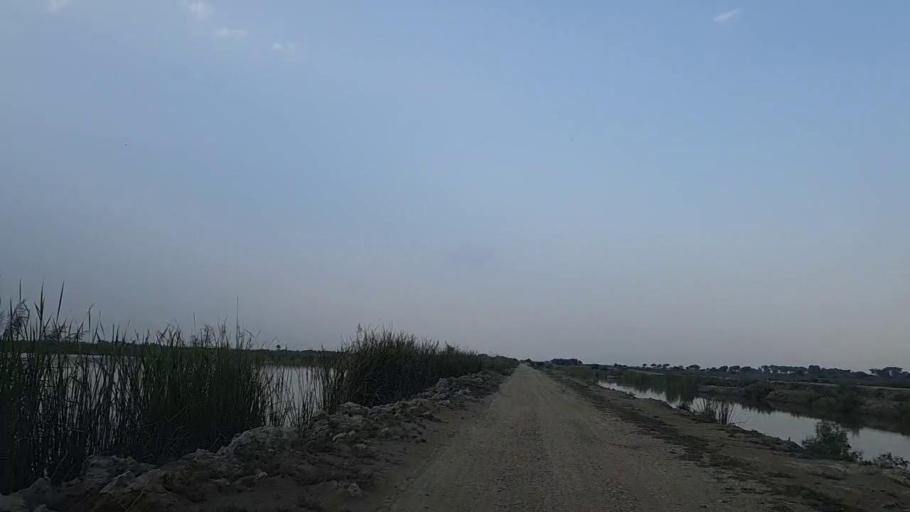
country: PK
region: Sindh
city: Daro Mehar
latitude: 24.7708
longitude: 68.1338
